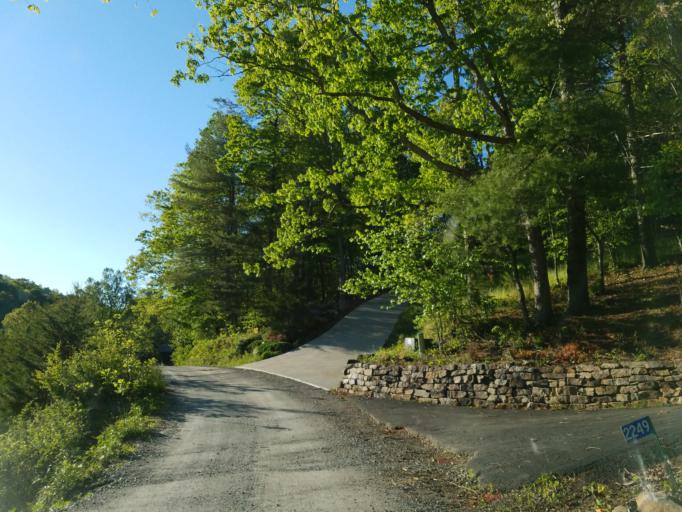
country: US
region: Georgia
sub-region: Fannin County
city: Blue Ridge
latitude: 34.7497
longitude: -84.2562
